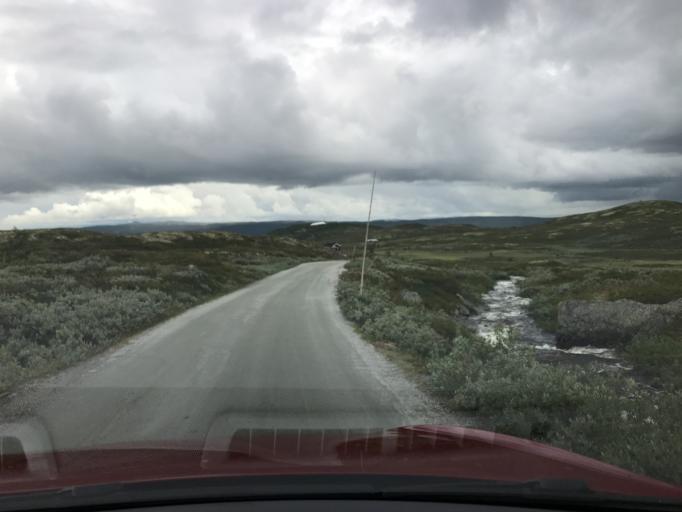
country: NO
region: Buskerud
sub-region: Hol
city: Geilo
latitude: 60.5464
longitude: 8.1608
